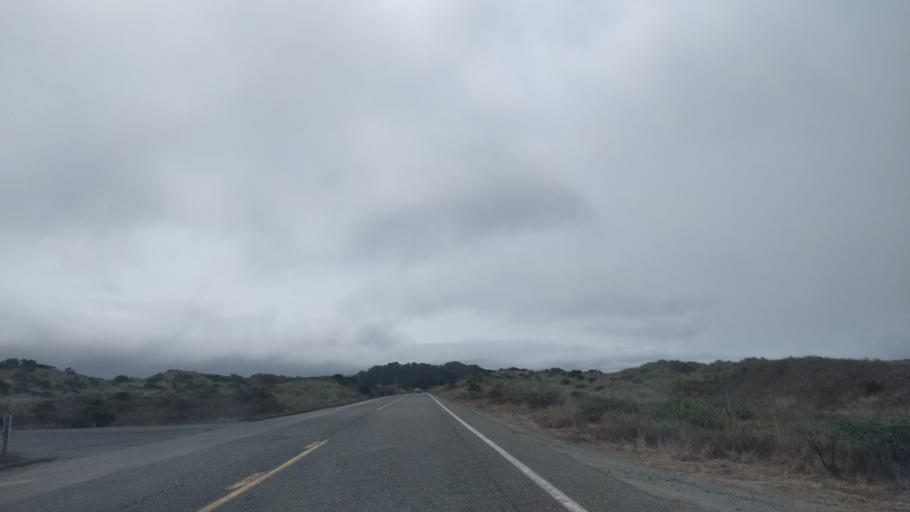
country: US
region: California
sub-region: Humboldt County
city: Bayview
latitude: 40.7884
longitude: -124.2068
